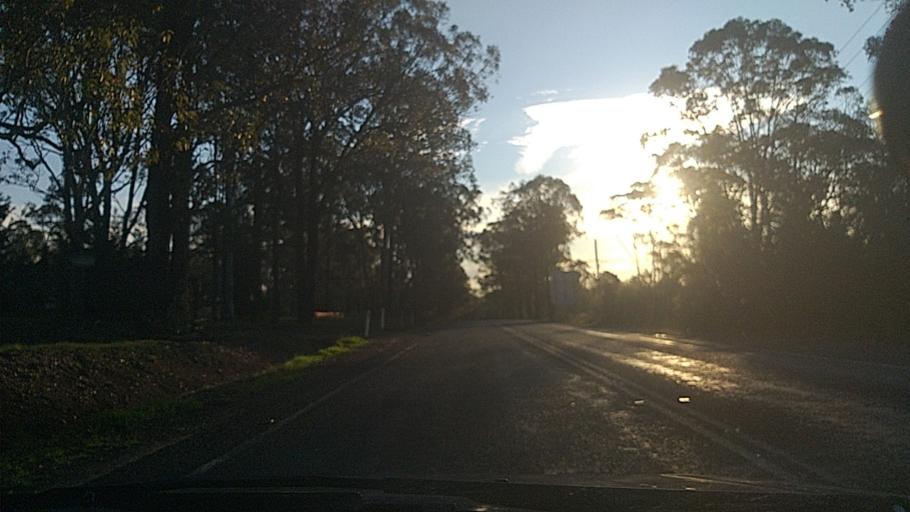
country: AU
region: New South Wales
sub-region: Wollondilly
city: Douglas Park
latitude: -34.2396
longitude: 150.7208
